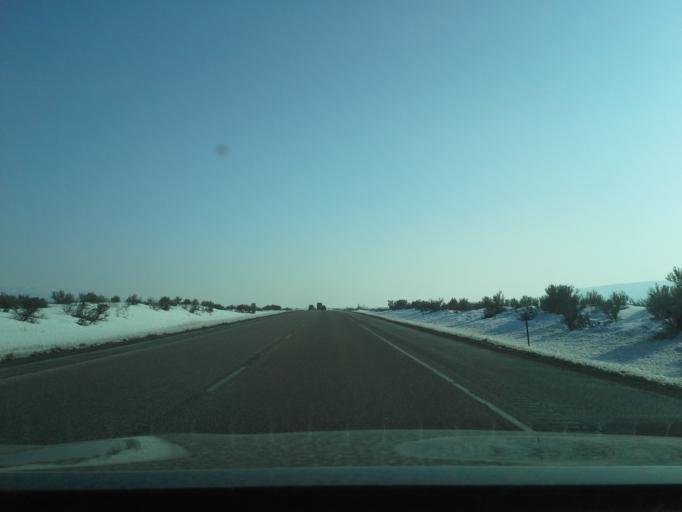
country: US
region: Idaho
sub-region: Bannock County
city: Pocatello
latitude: 42.7580
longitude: -112.2283
